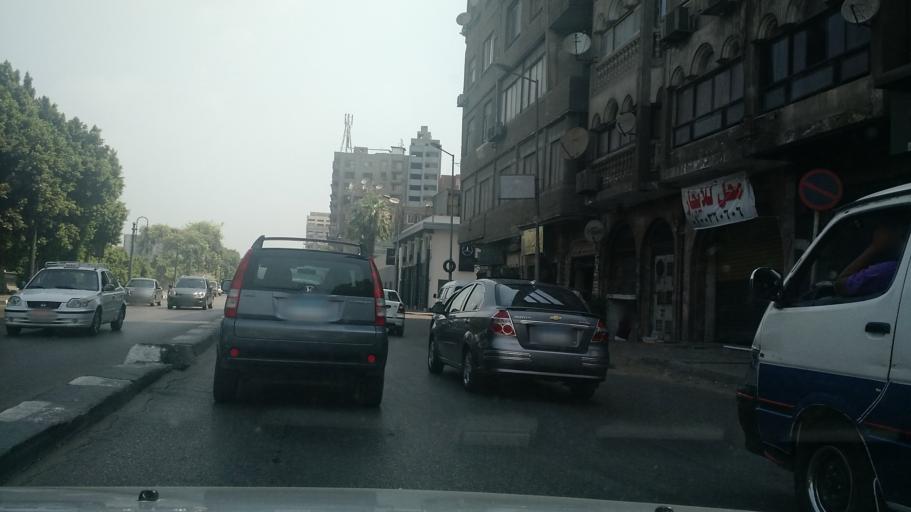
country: EG
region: Al Jizah
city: Al Jizah
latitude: 30.0186
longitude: 31.2294
